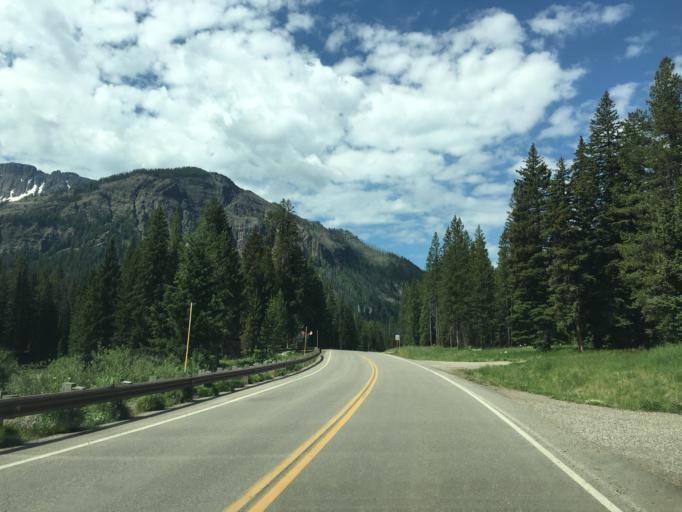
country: US
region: Montana
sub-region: Stillwater County
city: Absarokee
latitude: 45.0064
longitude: -109.9912
